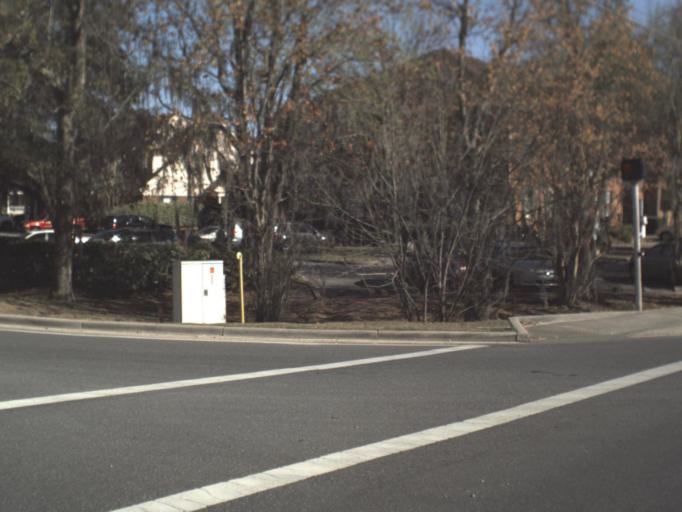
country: US
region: Florida
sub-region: Leon County
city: Tallahassee
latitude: 30.5003
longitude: -84.2474
